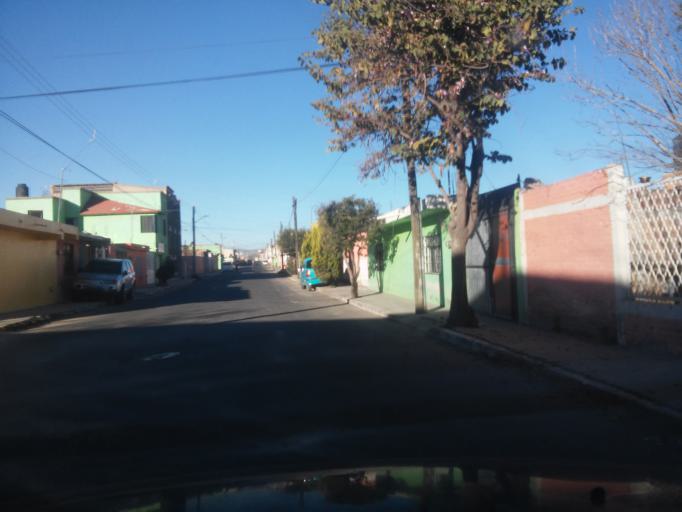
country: MX
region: Durango
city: Victoria de Durango
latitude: 24.0135
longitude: -104.6469
